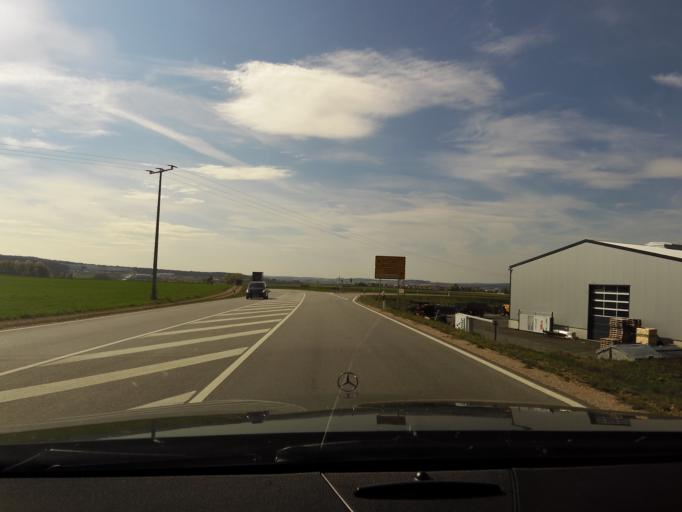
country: DE
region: Bavaria
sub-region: Upper Palatinate
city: Schierling
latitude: 48.8219
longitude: 12.1543
